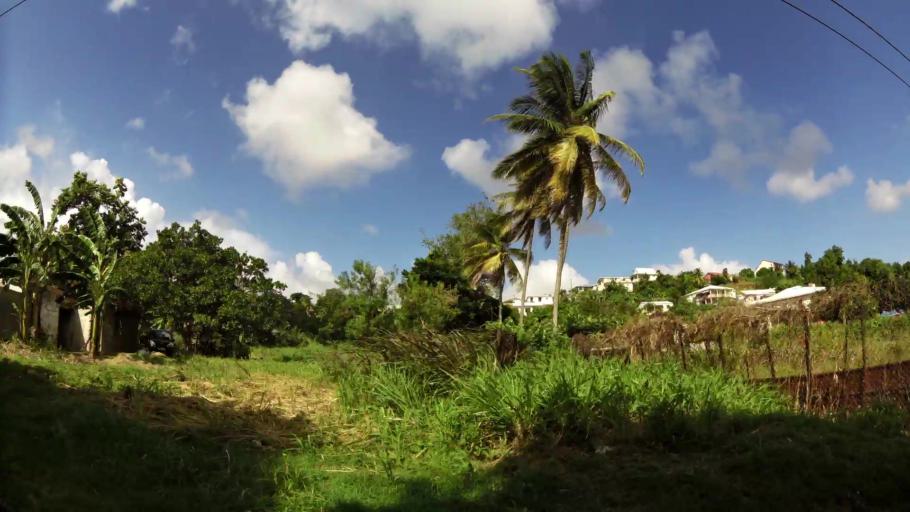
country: MQ
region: Martinique
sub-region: Martinique
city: Ducos
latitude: 14.5753
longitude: -60.9813
